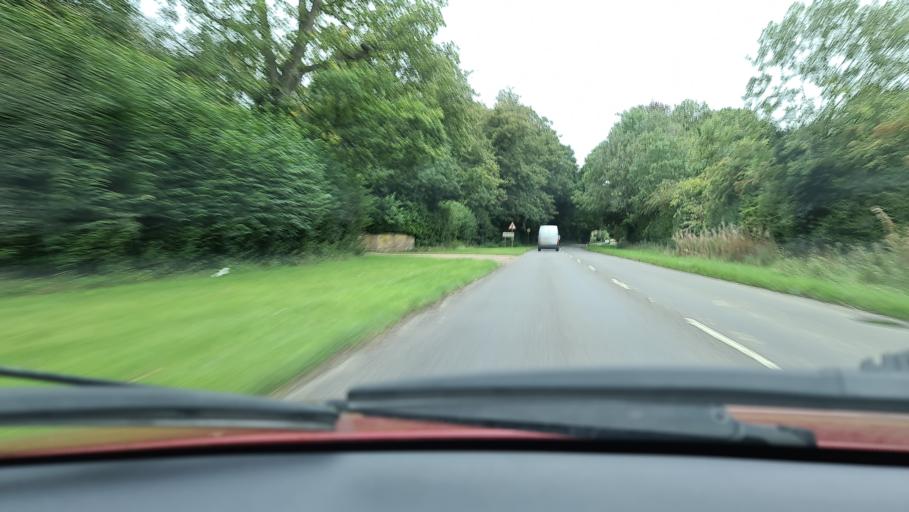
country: GB
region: England
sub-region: Buckinghamshire
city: Great Missenden
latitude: 51.7025
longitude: -0.6623
